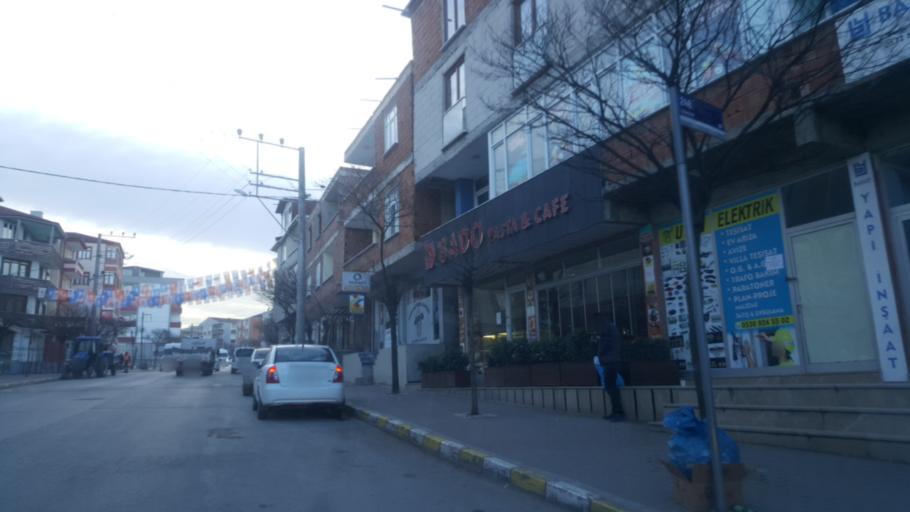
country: TR
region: Kocaeli
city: Tavsancil
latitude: 40.7910
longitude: 29.5469
